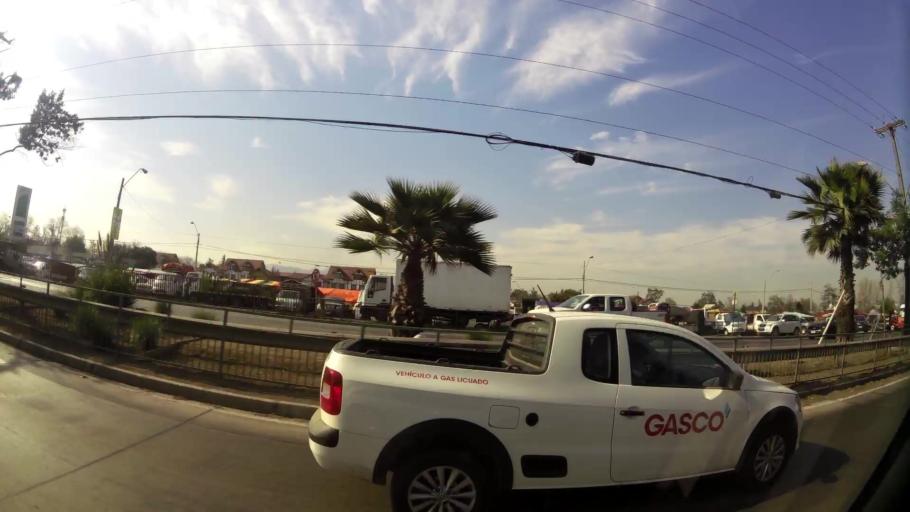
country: CL
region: Santiago Metropolitan
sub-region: Provincia de Talagante
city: Penaflor
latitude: -33.5547
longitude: -70.7968
